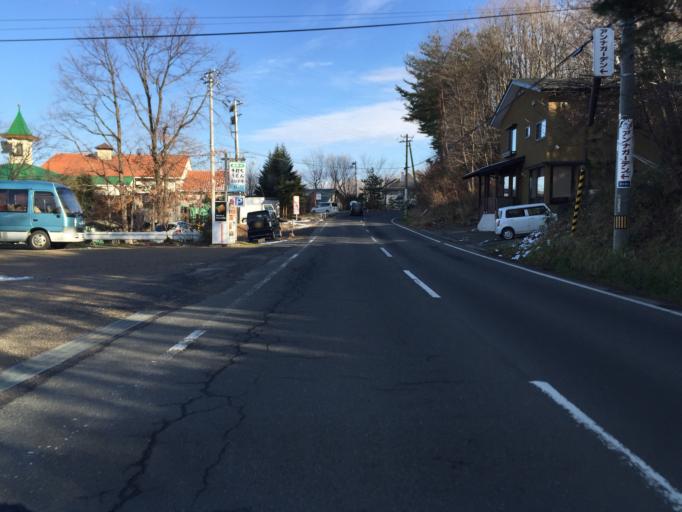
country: JP
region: Fukushima
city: Fukushima-shi
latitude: 37.7045
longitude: 140.3691
